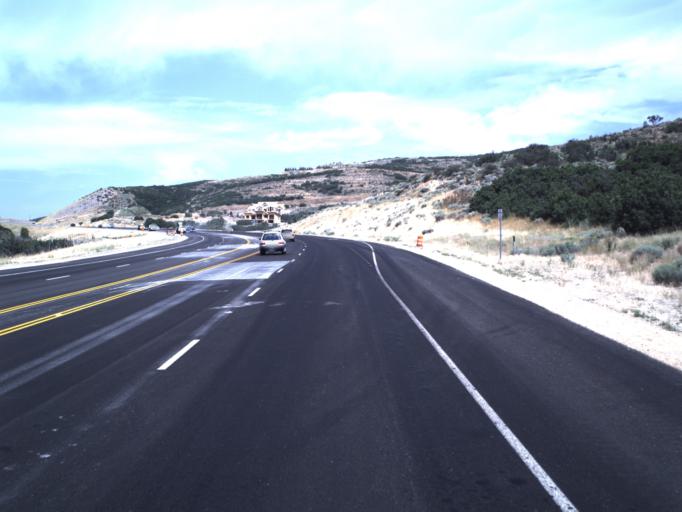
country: US
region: Utah
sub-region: Summit County
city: Park City
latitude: 40.6648
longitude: -111.4180
